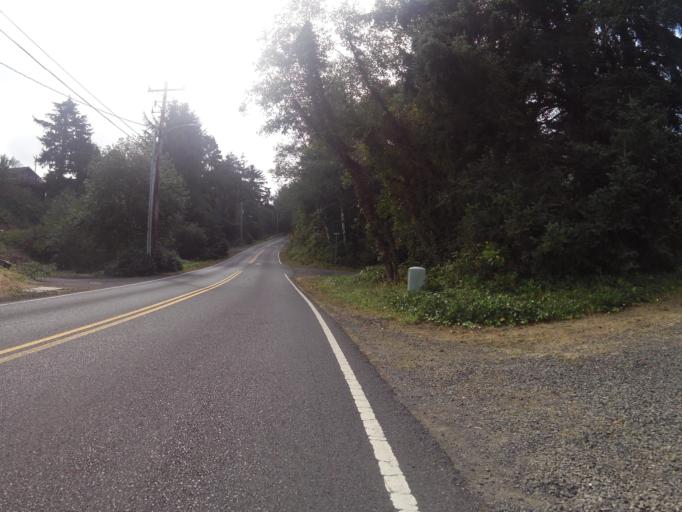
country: US
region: Oregon
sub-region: Lincoln County
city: Newport
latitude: 44.6519
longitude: -124.0565
